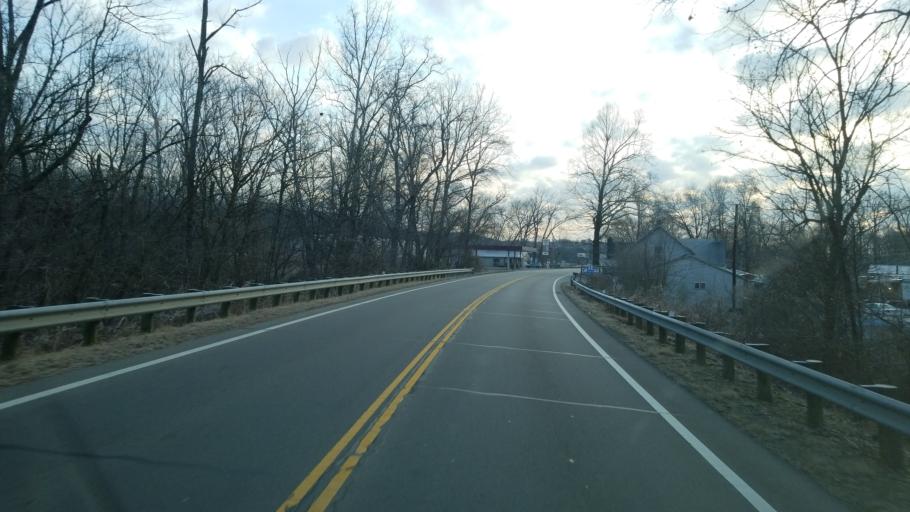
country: US
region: Ohio
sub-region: Ross County
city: North Fork Village
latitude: 39.3507
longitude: -83.0565
